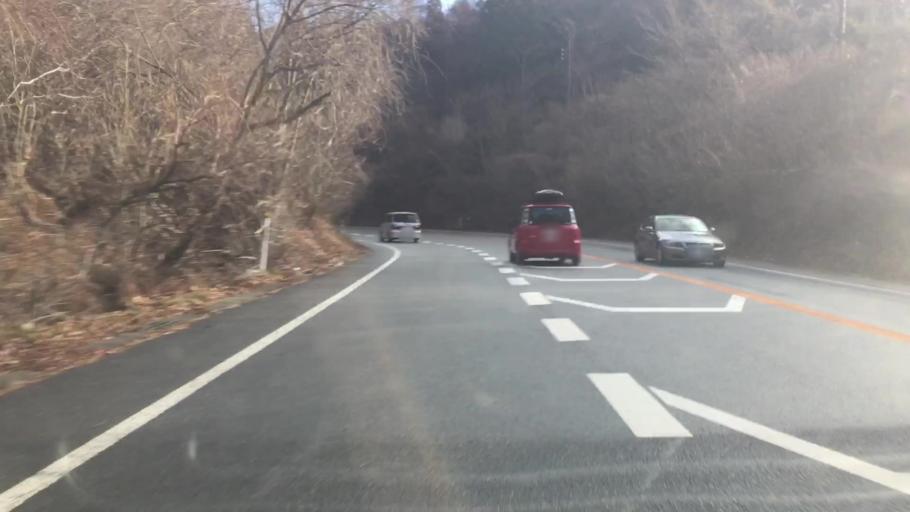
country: JP
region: Nagano
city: Saku
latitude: 36.3003
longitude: 138.6718
